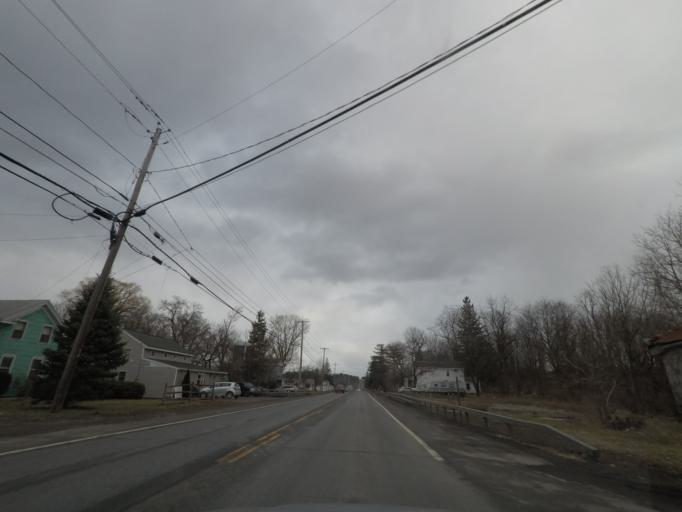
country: US
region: New York
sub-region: Madison County
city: Chittenango
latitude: 43.0544
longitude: -75.8464
